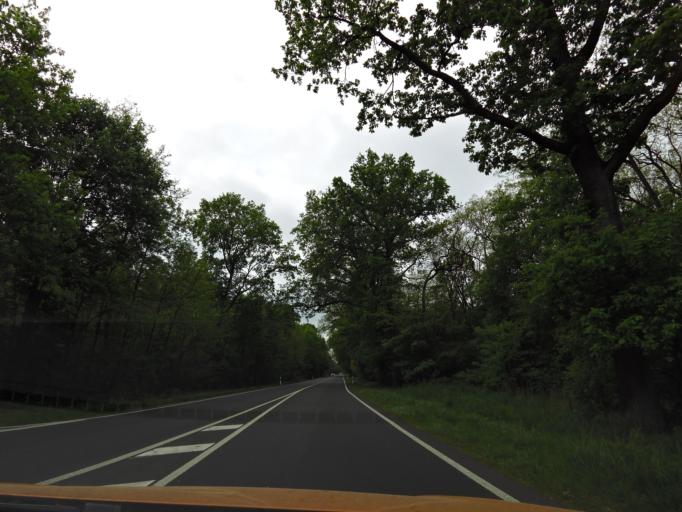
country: DE
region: Brandenburg
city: Michendorf
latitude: 52.2885
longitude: 13.0173
